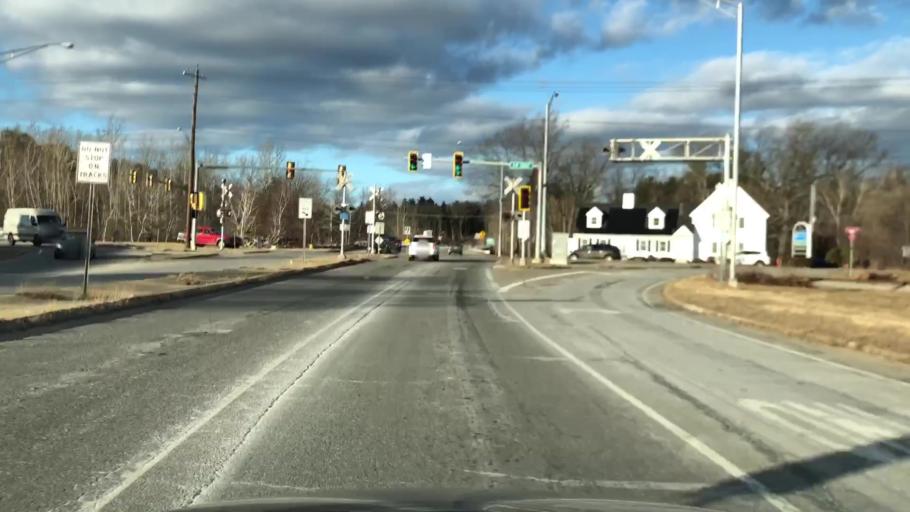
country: US
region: New Hampshire
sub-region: Hillsborough County
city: Wilton
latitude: 42.8417
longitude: -71.7033
